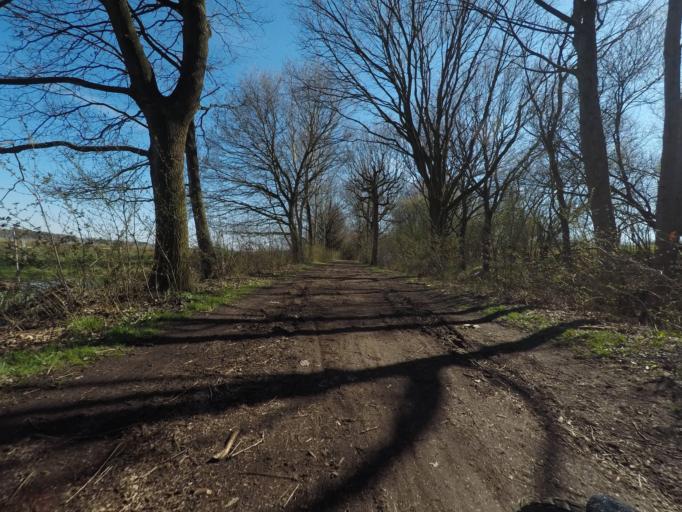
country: DE
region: Schleswig-Holstein
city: Norderstedt
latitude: 53.6591
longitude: 9.9699
